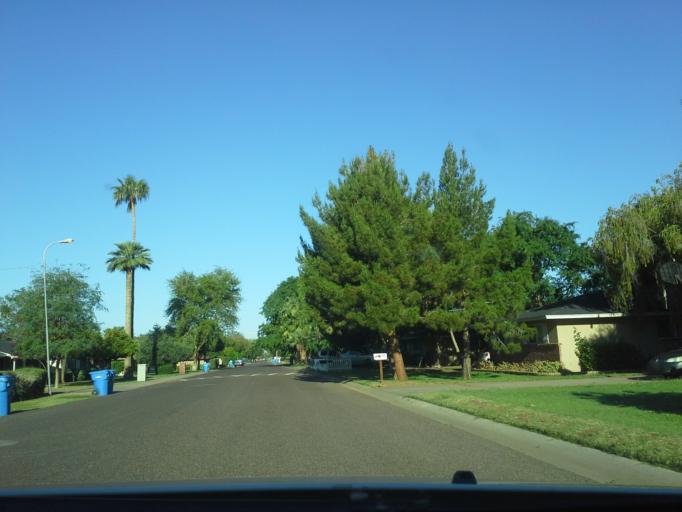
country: US
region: Arizona
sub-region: Maricopa County
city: Phoenix
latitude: 33.5421
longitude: -112.0853
